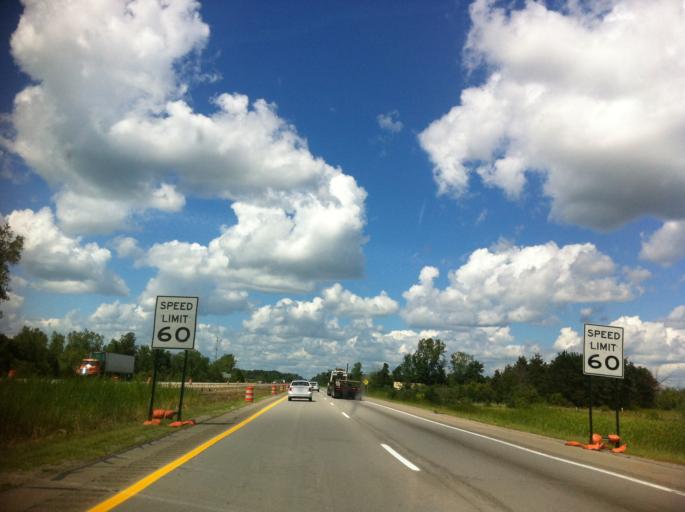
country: US
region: Michigan
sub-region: Washtenaw County
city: Milan
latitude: 42.1144
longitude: -83.6824
